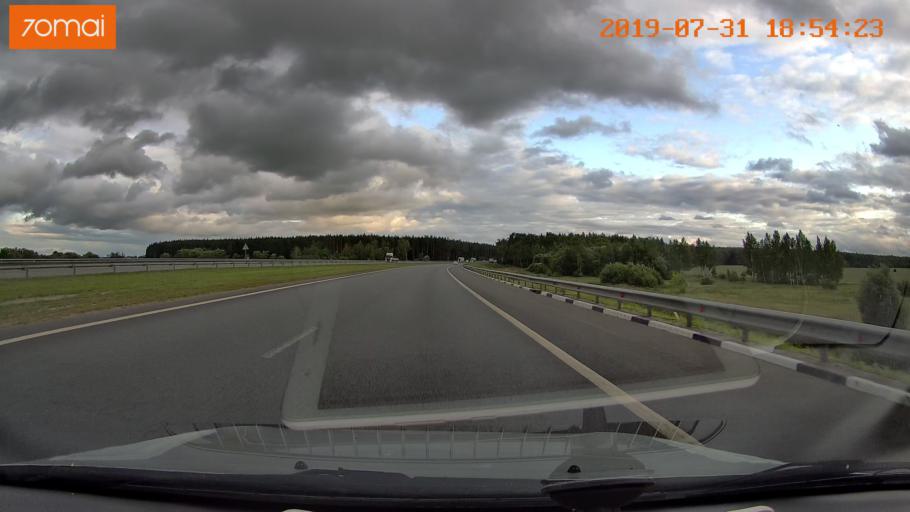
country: RU
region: Moskovskaya
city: Raduzhnyy
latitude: 55.1908
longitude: 38.6680
